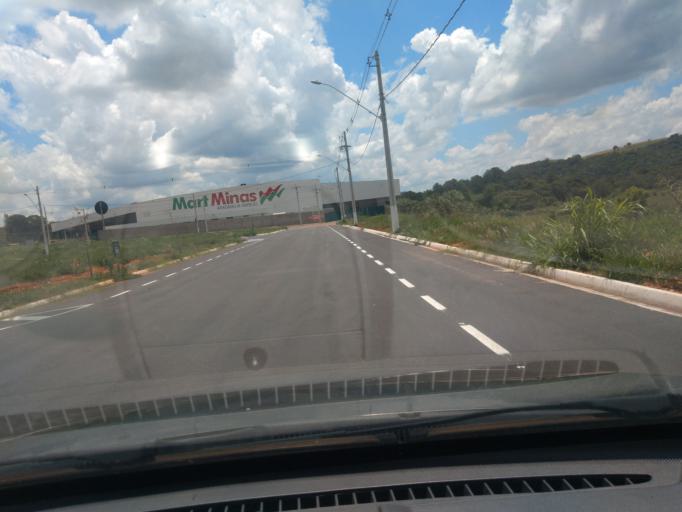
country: BR
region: Minas Gerais
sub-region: Tres Coracoes
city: Tres Coracoes
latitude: -21.6627
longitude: -45.2786
